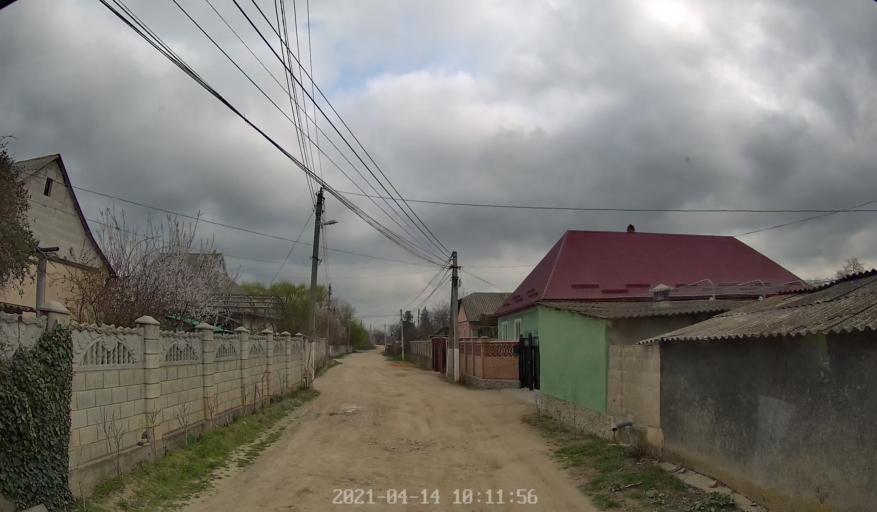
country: MD
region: Criuleni
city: Criuleni
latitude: 47.1470
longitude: 29.1294
